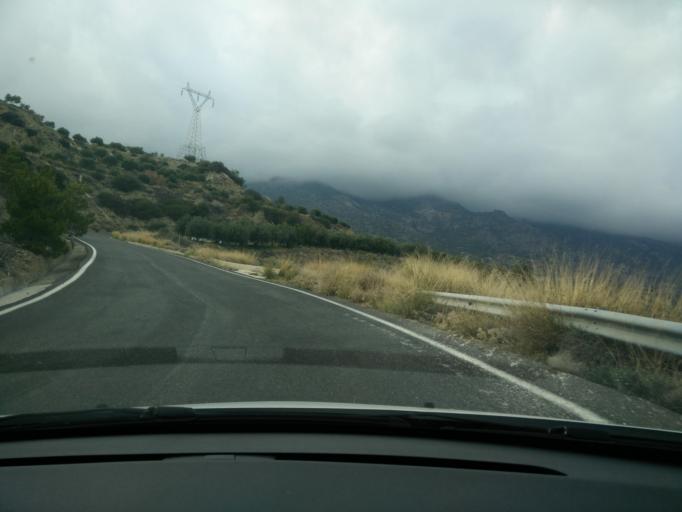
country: GR
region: Crete
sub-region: Nomos Lasithiou
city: Gra Liyia
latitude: 35.0192
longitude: 25.5799
